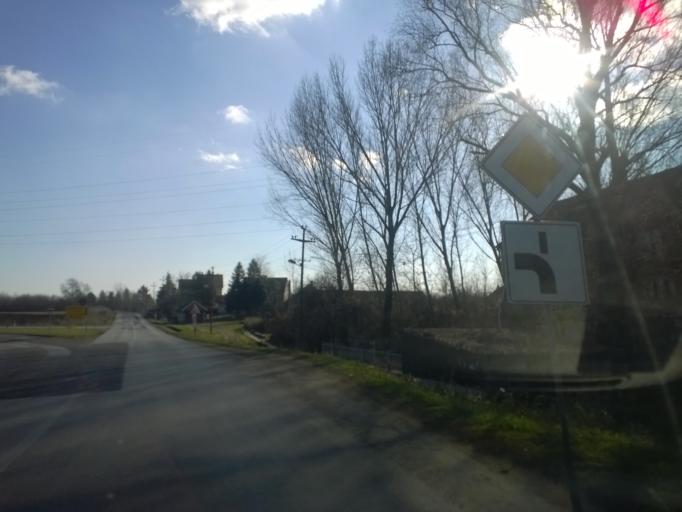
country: RS
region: Central Serbia
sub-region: Podunavski Okrug
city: Smederevo
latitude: 44.5892
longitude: 20.9723
